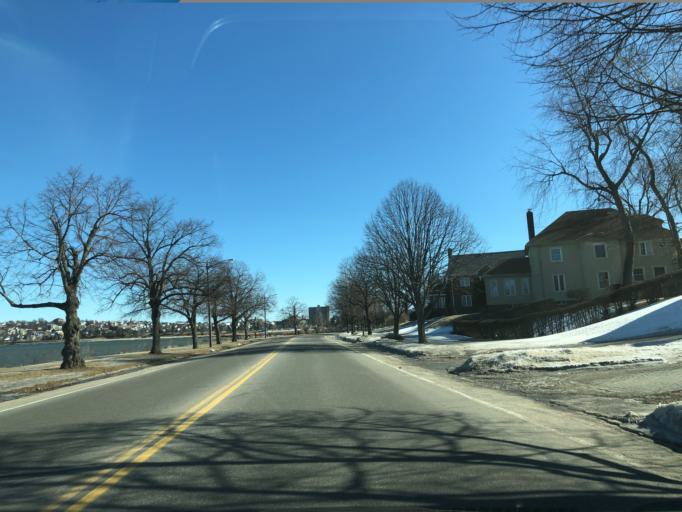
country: US
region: Maine
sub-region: Cumberland County
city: Portland
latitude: 43.6664
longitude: -70.2733
